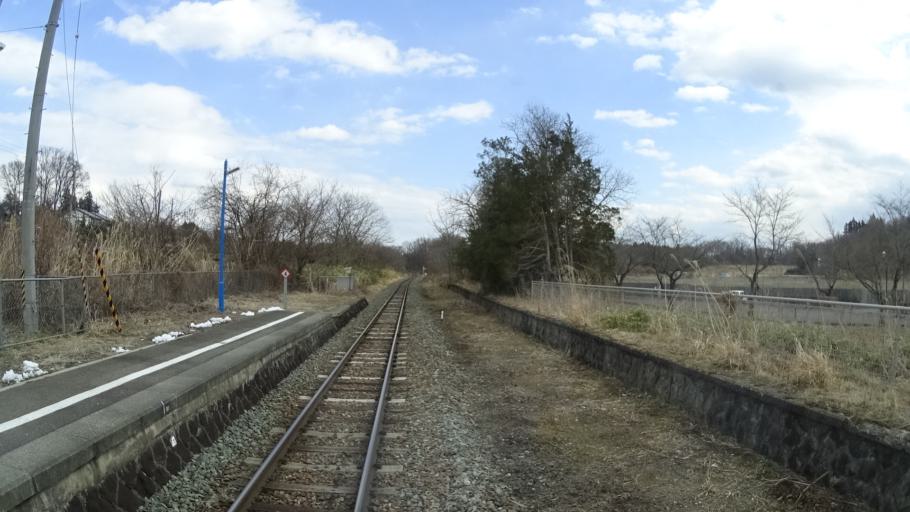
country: JP
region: Iwate
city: Hanamaki
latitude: 39.4085
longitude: 141.1942
